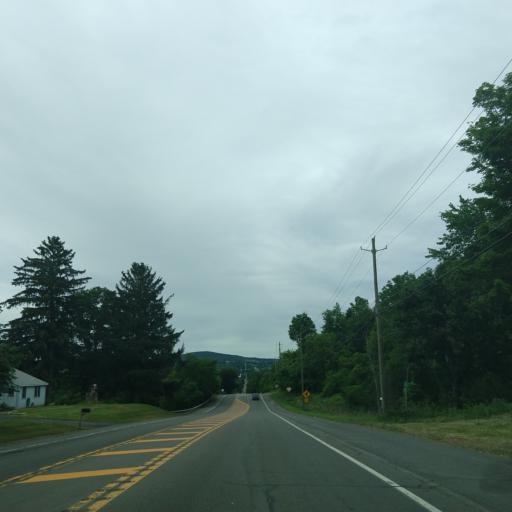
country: US
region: New York
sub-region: Tompkins County
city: Dryden
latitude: 42.4899
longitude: -76.3177
